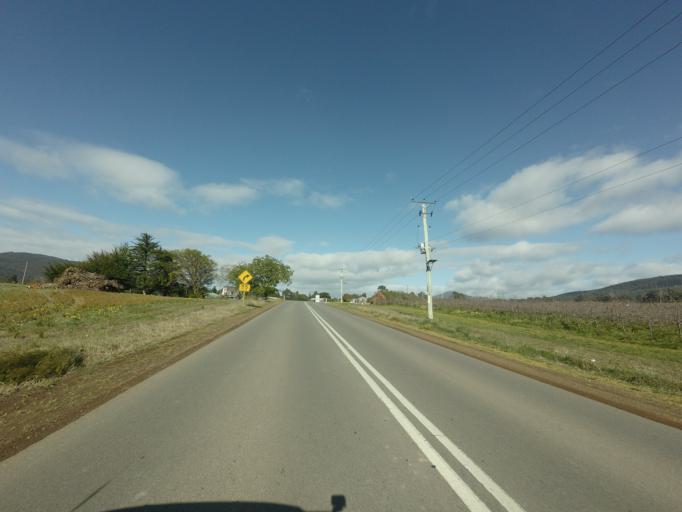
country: AU
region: Tasmania
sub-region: Huon Valley
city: Geeveston
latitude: -43.3227
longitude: 146.9999
